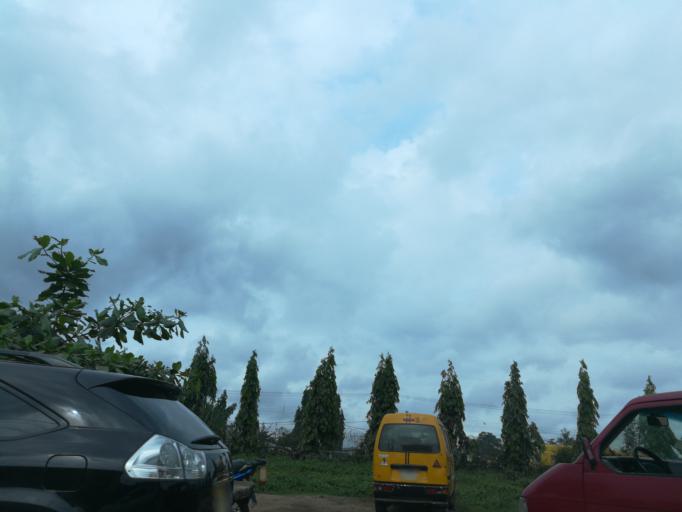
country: NG
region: Lagos
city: Ikeja
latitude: 6.5992
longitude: 3.3346
